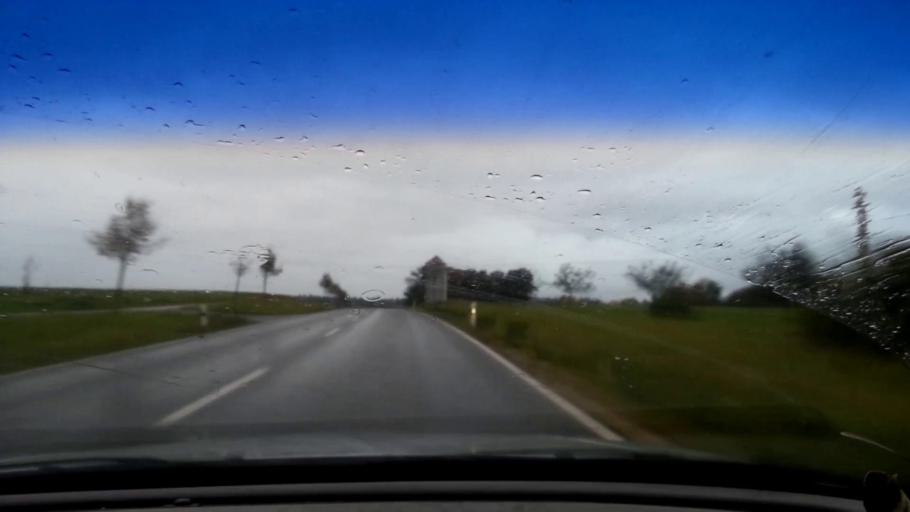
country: DE
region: Bavaria
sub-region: Upper Franconia
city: Walsdorf
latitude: 49.8825
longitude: 10.7843
